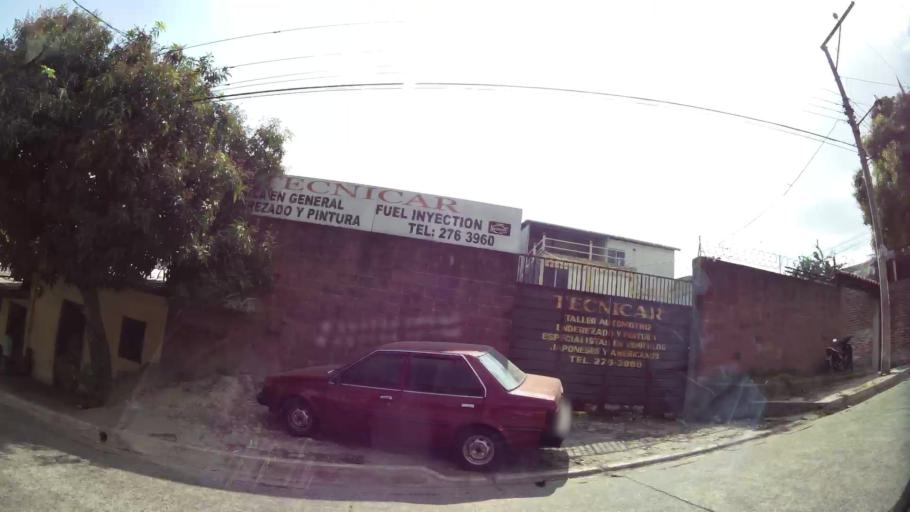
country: SV
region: San Salvador
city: Delgado
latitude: 13.7111
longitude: -89.1701
